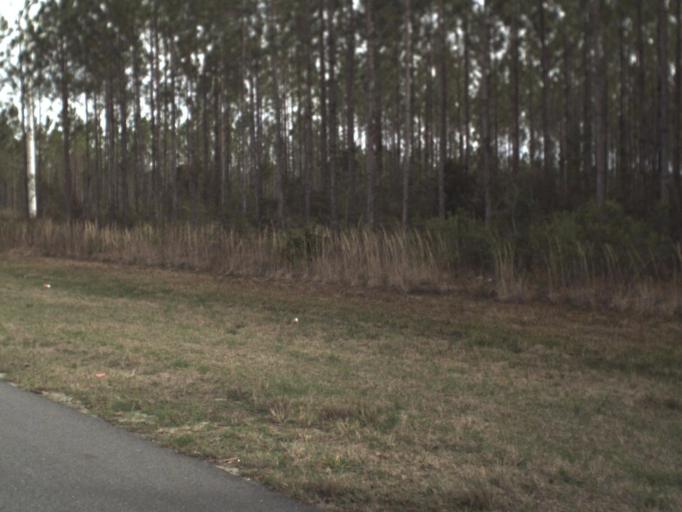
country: US
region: Florida
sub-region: Bay County
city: Callaway
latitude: 30.1494
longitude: -85.4678
